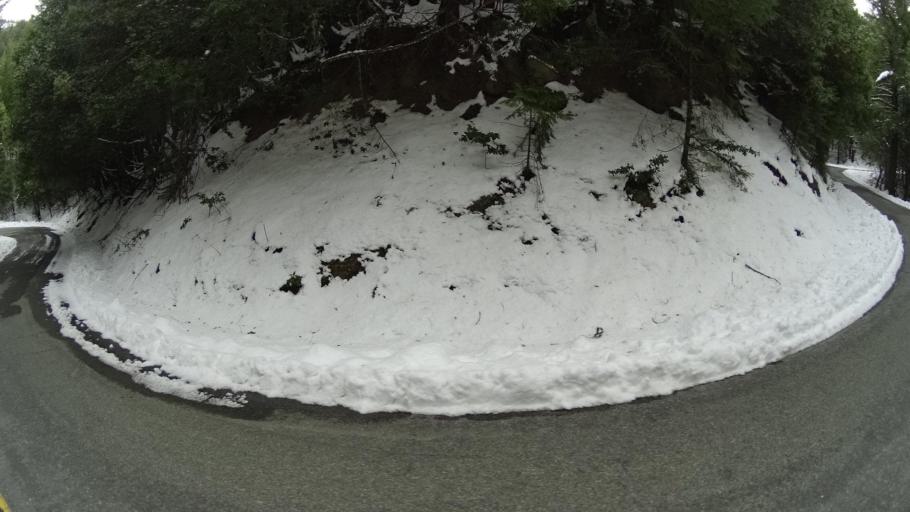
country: US
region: California
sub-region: Humboldt County
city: Willow Creek
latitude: 40.8660
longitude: -123.7418
